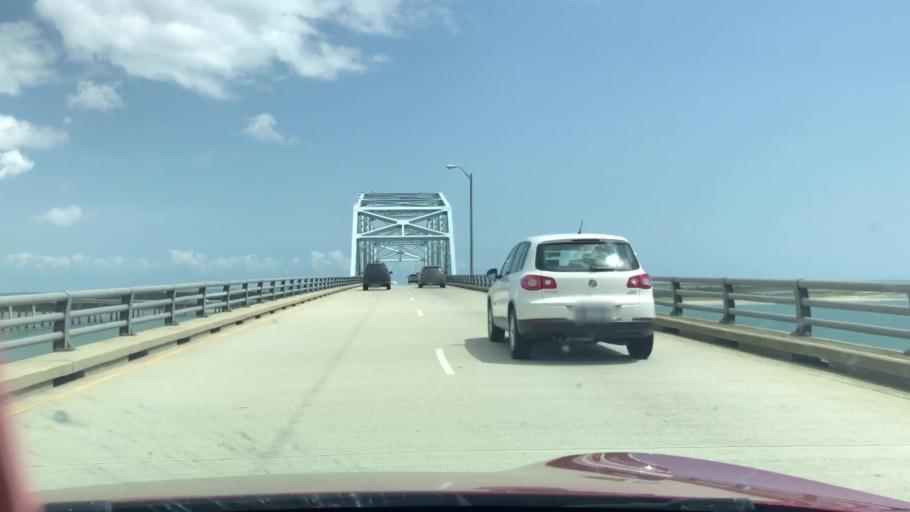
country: US
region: Virginia
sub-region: Northampton County
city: Cape Charles
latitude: 37.0883
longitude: -75.9893
